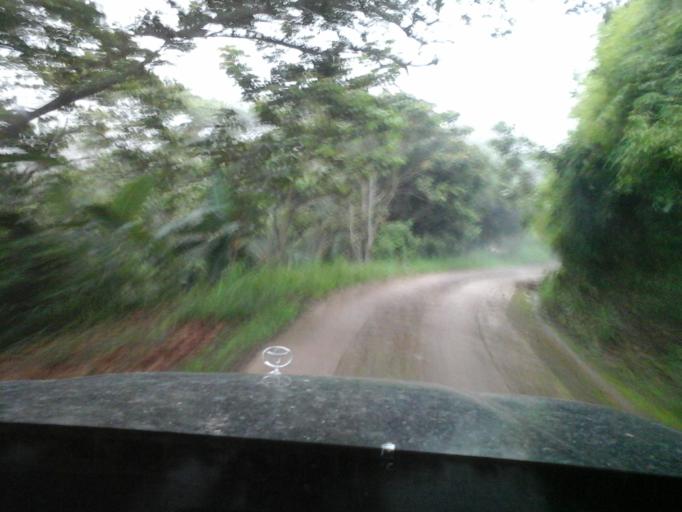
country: CO
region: Cesar
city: Agustin Codazzi
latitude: 9.9411
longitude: -73.1290
